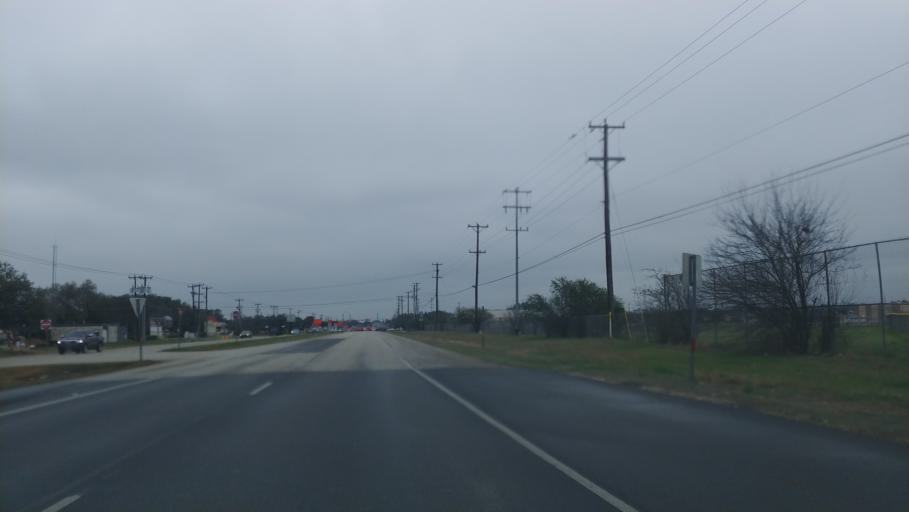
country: US
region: Texas
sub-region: Bexar County
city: Helotes
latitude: 29.5626
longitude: -98.6845
